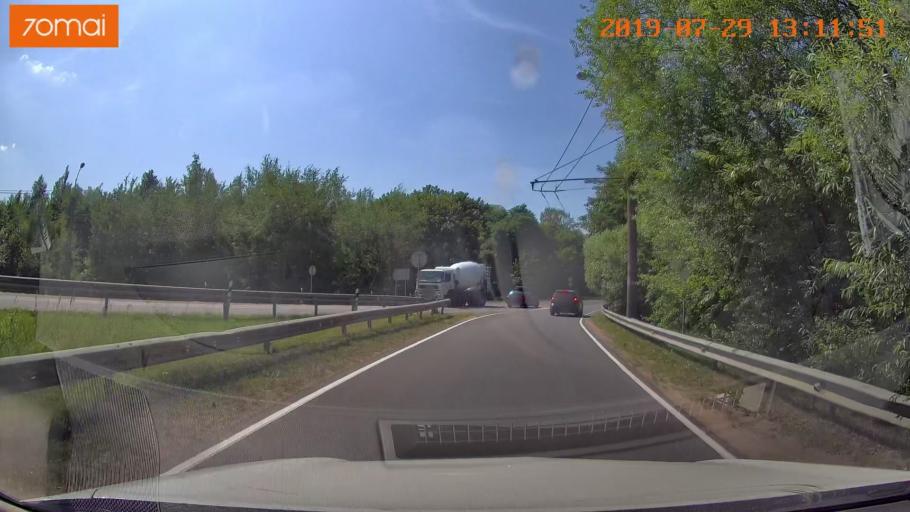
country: RU
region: Kaliningrad
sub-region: Gorod Kaliningrad
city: Kaliningrad
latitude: 54.7182
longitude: 20.3842
